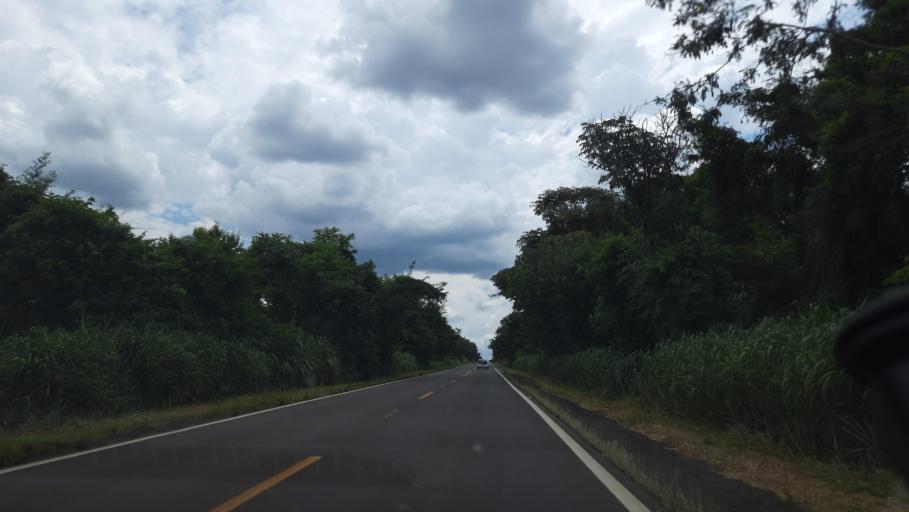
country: BR
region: Sao Paulo
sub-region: Mococa
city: Mococa
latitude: -21.4615
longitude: -47.1092
